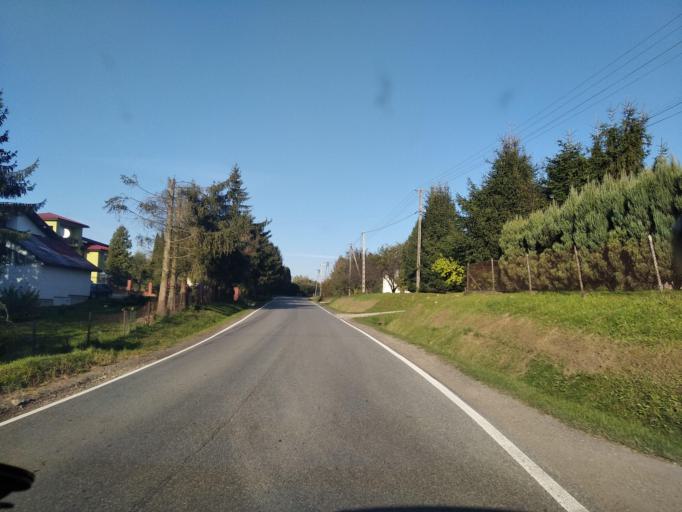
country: PL
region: Subcarpathian Voivodeship
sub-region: Powiat brzozowski
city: Turze Pole
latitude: 49.6601
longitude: 21.9990
